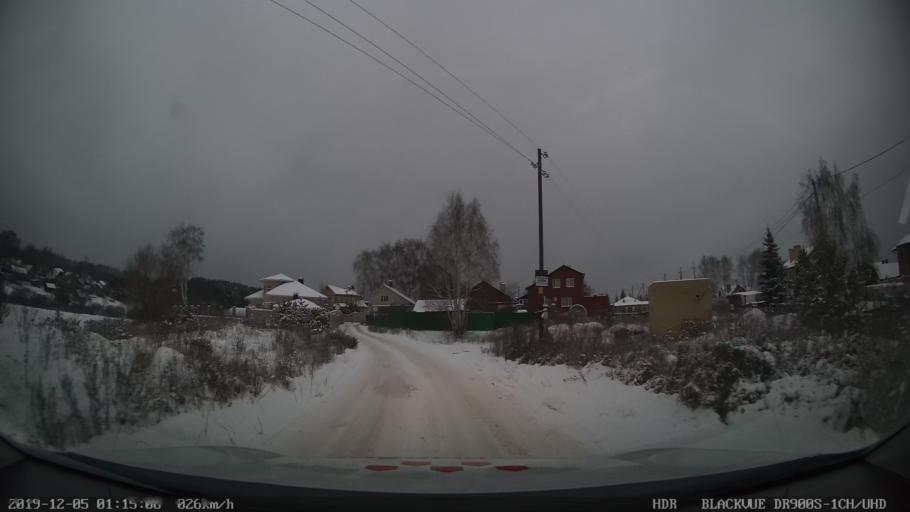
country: RU
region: Tatarstan
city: Stolbishchi
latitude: 55.6451
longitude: 49.1138
